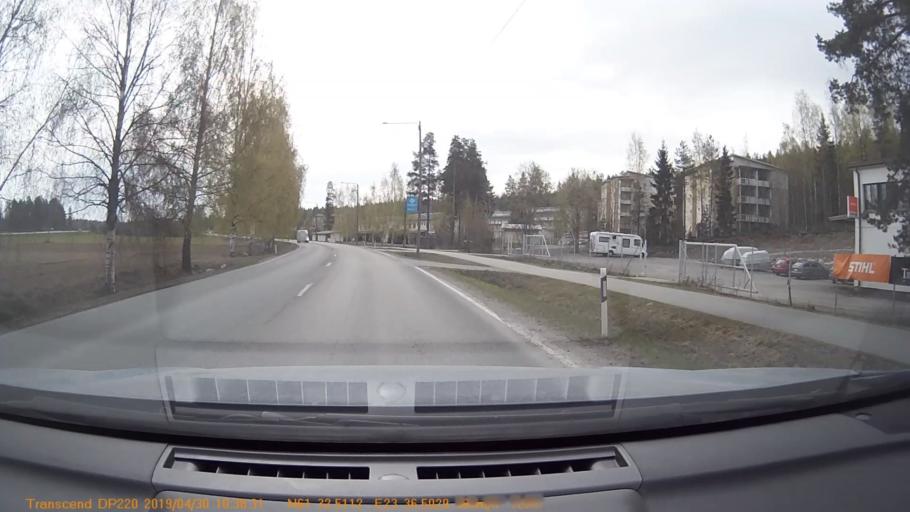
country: FI
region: Pirkanmaa
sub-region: Tampere
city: Yloejaervi
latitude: 61.5419
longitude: 23.6081
